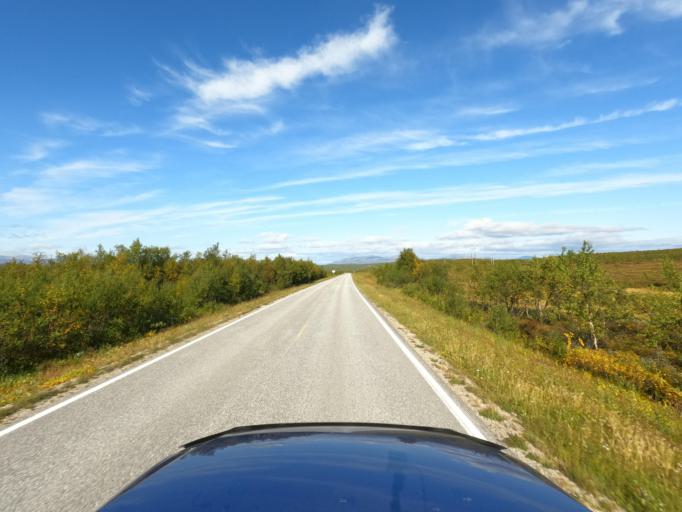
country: NO
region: Finnmark Fylke
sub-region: Karasjok
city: Karasjohka
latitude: 69.7275
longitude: 25.2344
